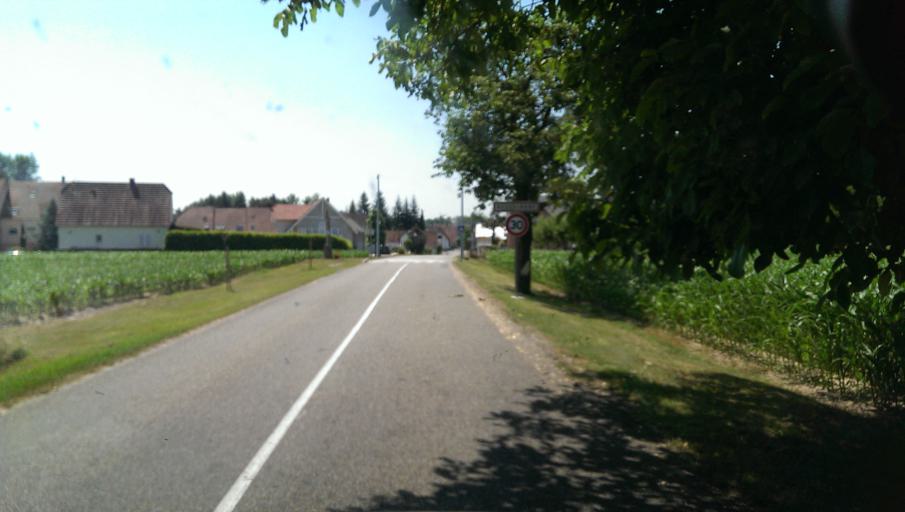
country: FR
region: Alsace
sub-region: Departement du Bas-Rhin
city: Seltz
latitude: 48.8805
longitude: 8.0713
